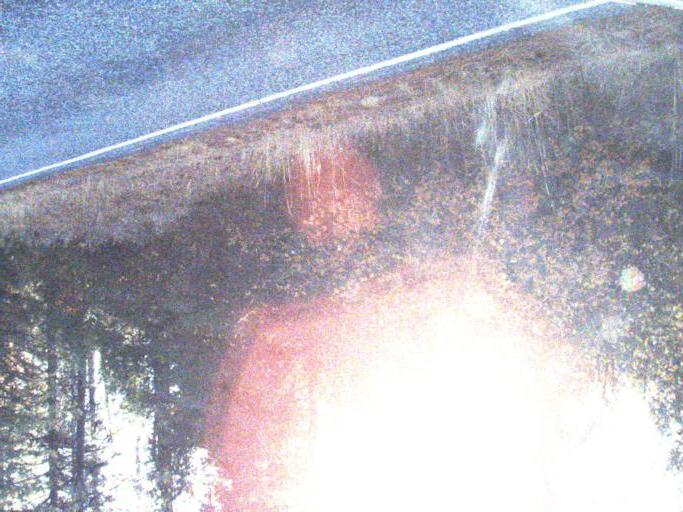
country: US
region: Washington
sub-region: Okanogan County
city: Coulee Dam
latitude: 48.0571
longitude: -118.6717
